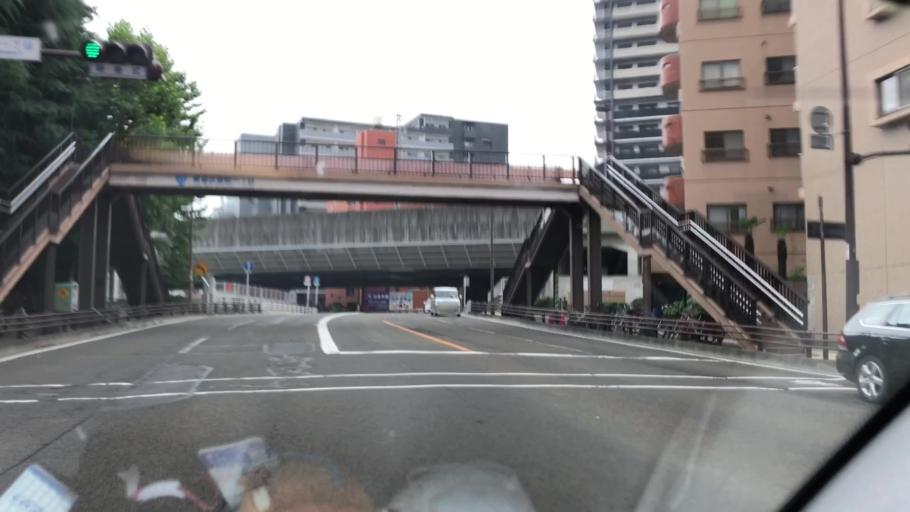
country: JP
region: Miyagi
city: Sendai-shi
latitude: 38.2653
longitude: 140.8834
